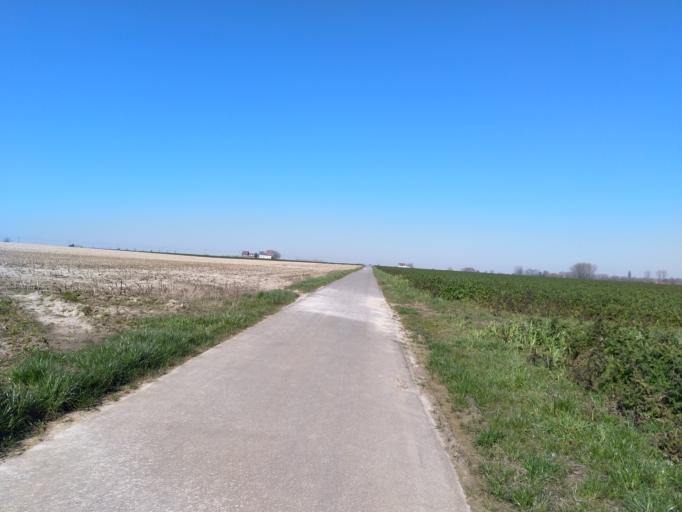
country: BE
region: Wallonia
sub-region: Province du Hainaut
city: Soignies
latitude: 50.5695
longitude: 3.9956
